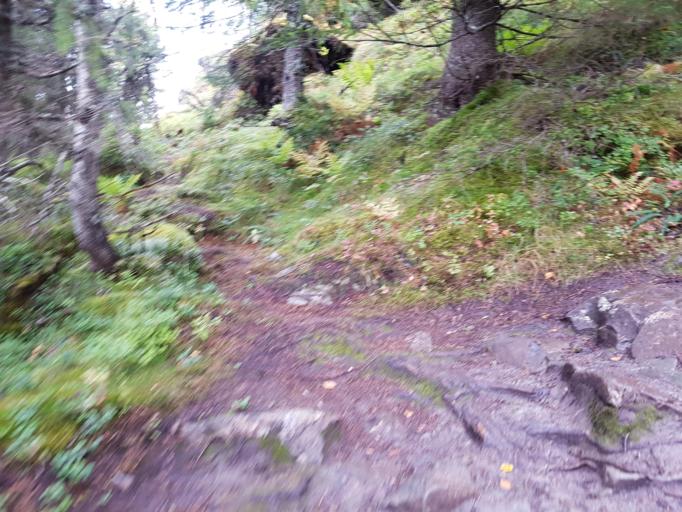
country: NO
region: Sor-Trondelag
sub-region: Melhus
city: Melhus
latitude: 63.4061
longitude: 10.2050
